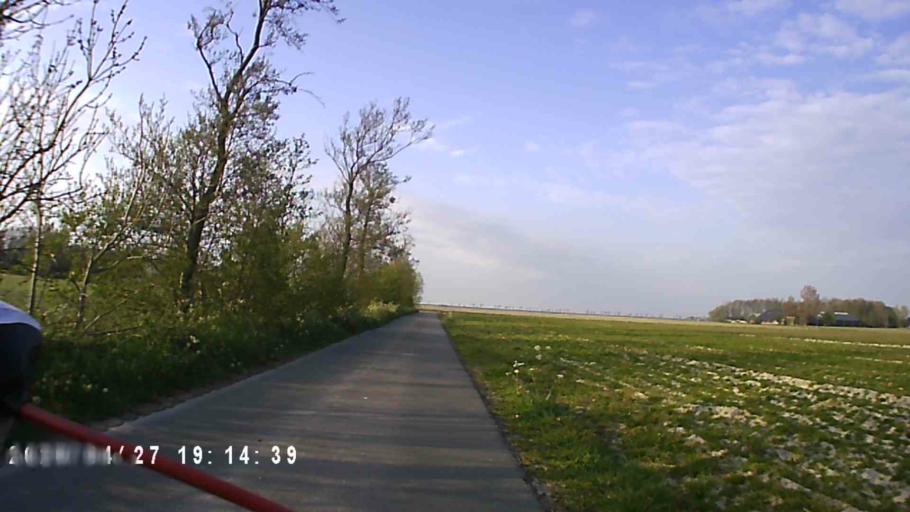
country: NL
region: Groningen
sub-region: Gemeente Winsum
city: Winsum
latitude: 53.4036
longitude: 6.4652
